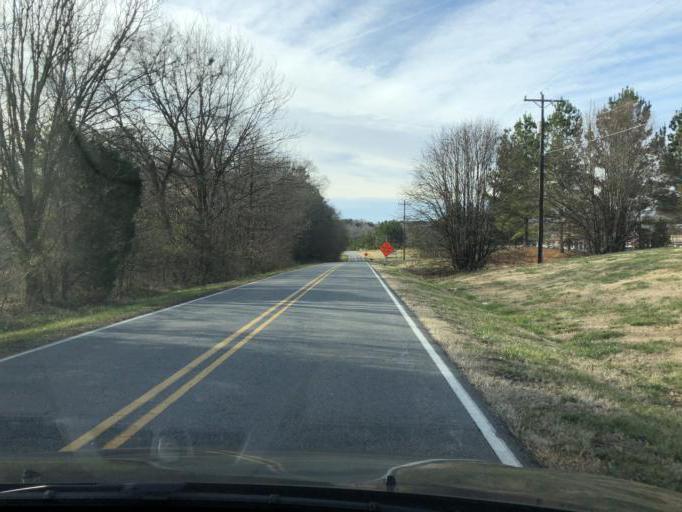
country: US
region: North Carolina
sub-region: Cleveland County
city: Boiling Springs
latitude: 35.2481
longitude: -81.6450
